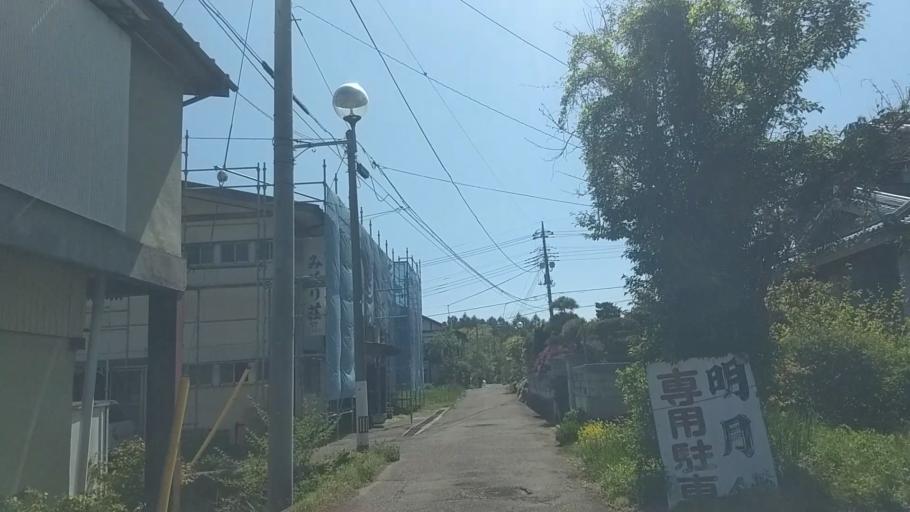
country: JP
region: Yamanashi
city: Nirasaki
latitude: 35.9180
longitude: 138.4378
